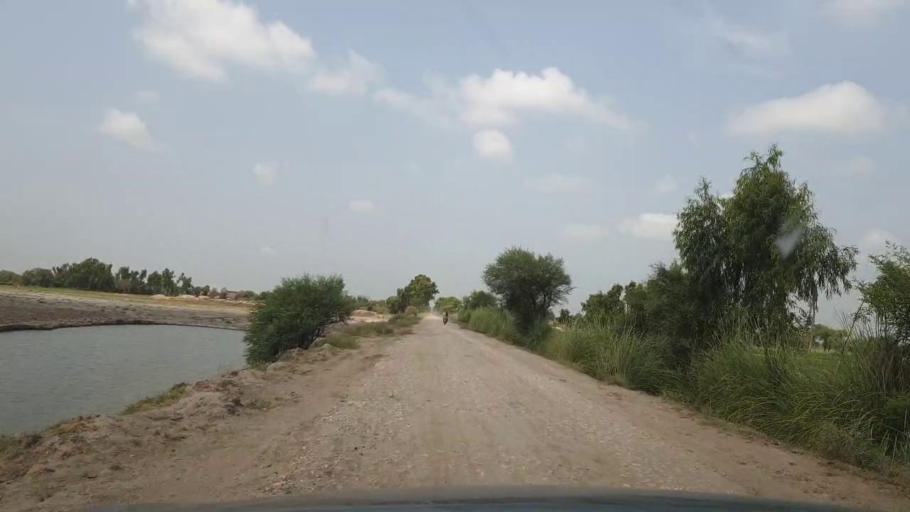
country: PK
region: Sindh
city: Ratodero
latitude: 27.8908
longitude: 68.2974
